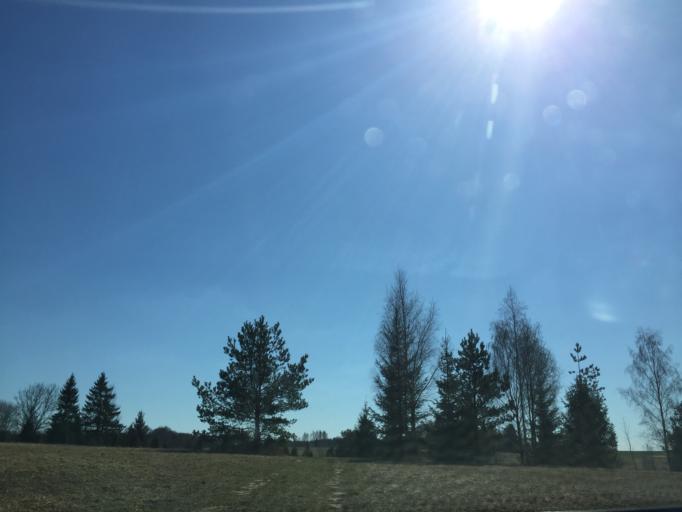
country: EE
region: Viljandimaa
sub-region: Viiratsi vald
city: Viiratsi
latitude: 58.3122
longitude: 25.6840
